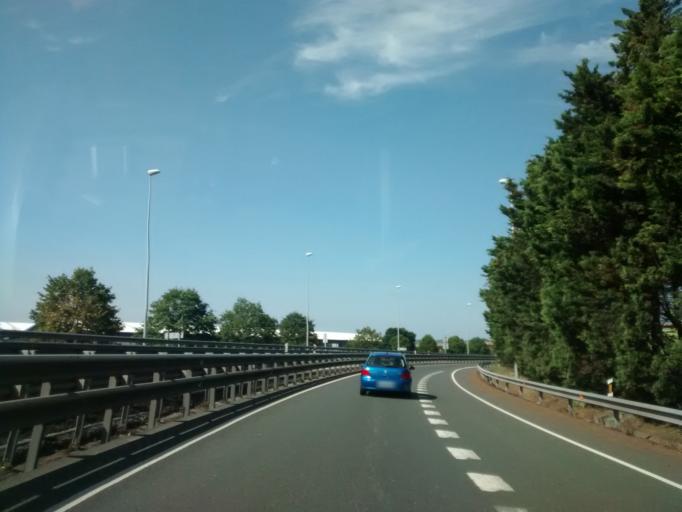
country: ES
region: Cantabria
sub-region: Provincia de Cantabria
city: El Astillero
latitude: 43.4368
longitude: -3.8338
